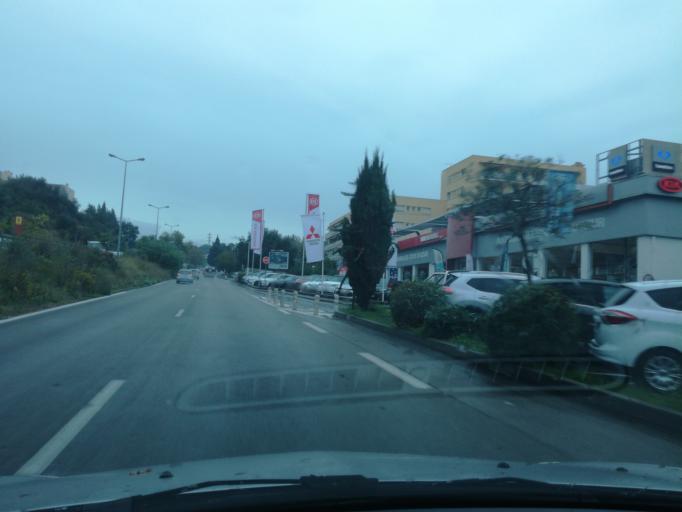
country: FR
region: Provence-Alpes-Cote d'Azur
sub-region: Departement des Alpes-Maritimes
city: Le Cannet
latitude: 43.5782
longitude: 7.0121
